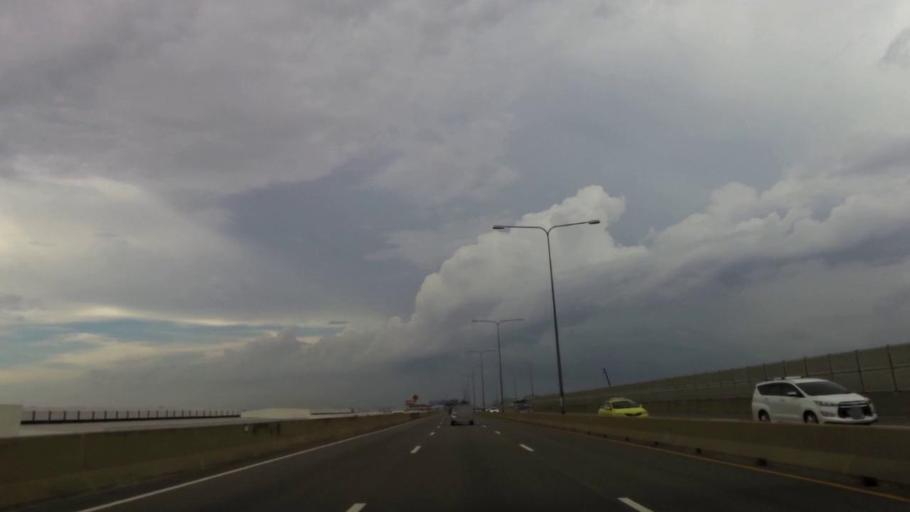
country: TH
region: Bangkok
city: Don Mueang
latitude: 13.9032
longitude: 100.5920
